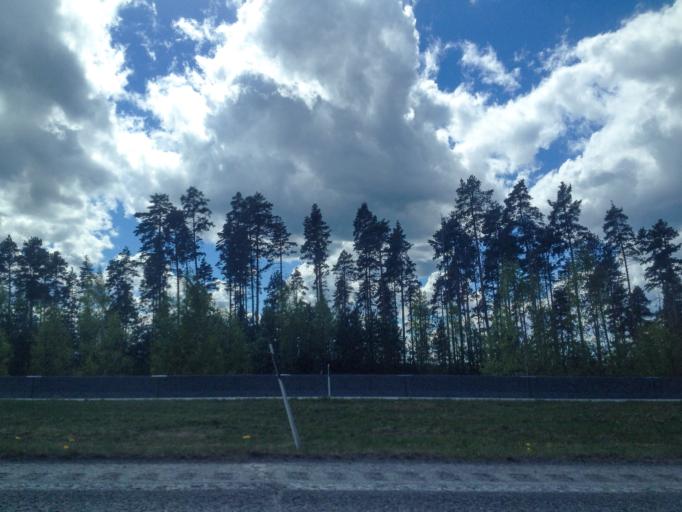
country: FI
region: Haeme
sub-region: Haemeenlinna
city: Parola
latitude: 61.0620
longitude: 24.3313
